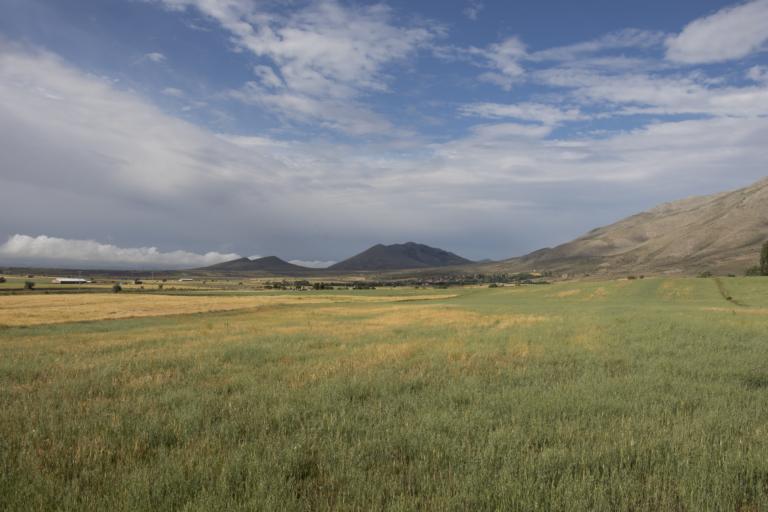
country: TR
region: Kayseri
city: Toklar
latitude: 38.4226
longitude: 36.0889
